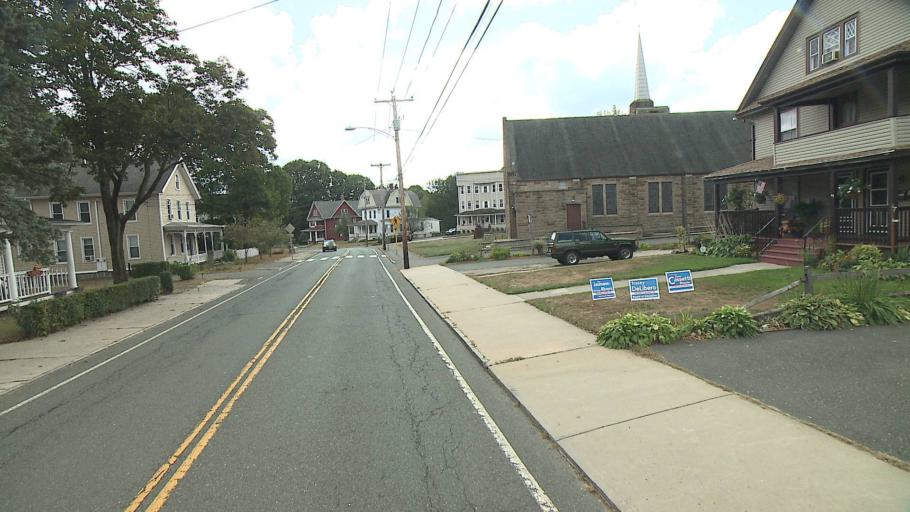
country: US
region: Connecticut
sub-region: New Haven County
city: Ansonia
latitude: 41.3476
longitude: -73.0874
